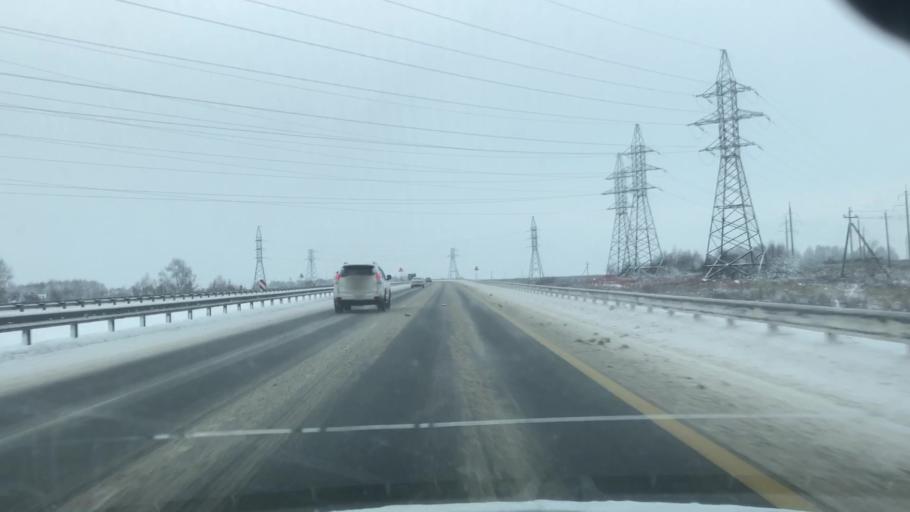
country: RU
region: Moskovskaya
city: Mikhnevo
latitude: 55.1215
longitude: 37.9308
